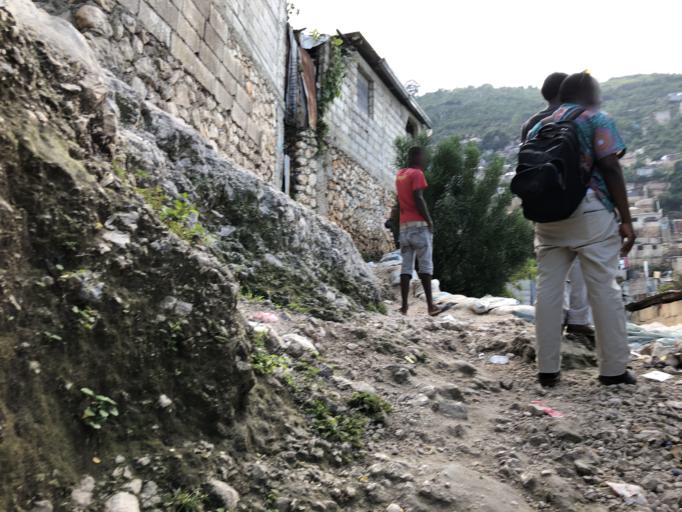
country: HT
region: Ouest
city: Port-au-Prince
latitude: 18.5204
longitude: -72.3157
